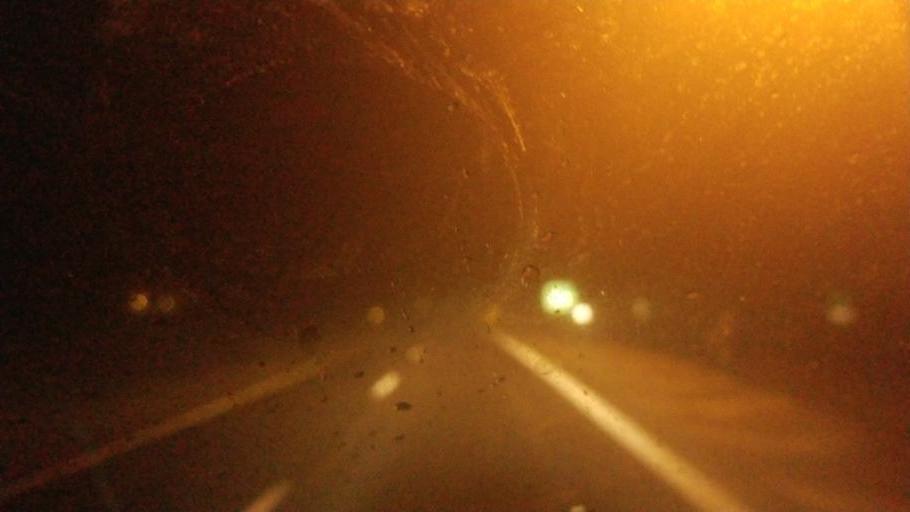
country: US
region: New York
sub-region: Cattaraugus County
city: Saint Bonaventure
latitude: 42.0883
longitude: -78.4572
